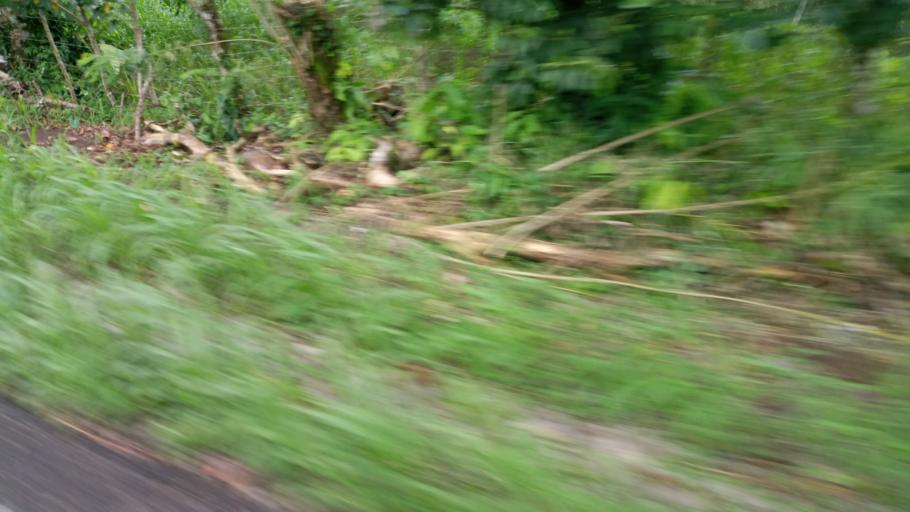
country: CR
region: Alajuela
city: Pocosol
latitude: 10.3748
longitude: -84.5553
